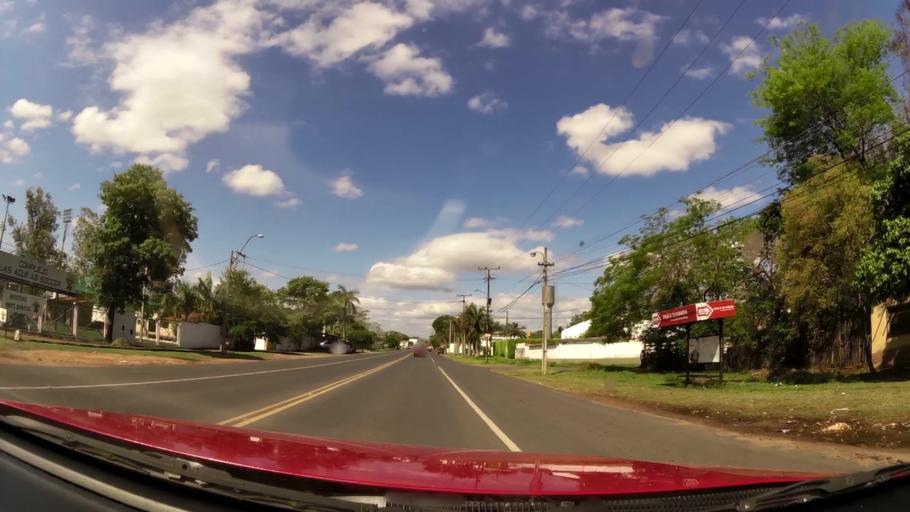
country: PY
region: Central
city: Fernando de la Mora
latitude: -25.2644
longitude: -57.5185
